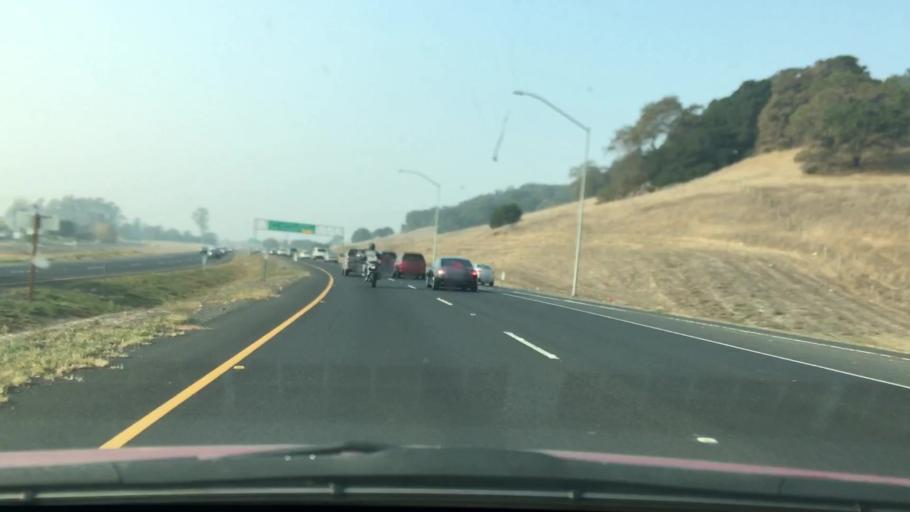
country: US
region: California
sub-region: Napa County
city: American Canyon
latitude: 38.2341
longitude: -122.2601
